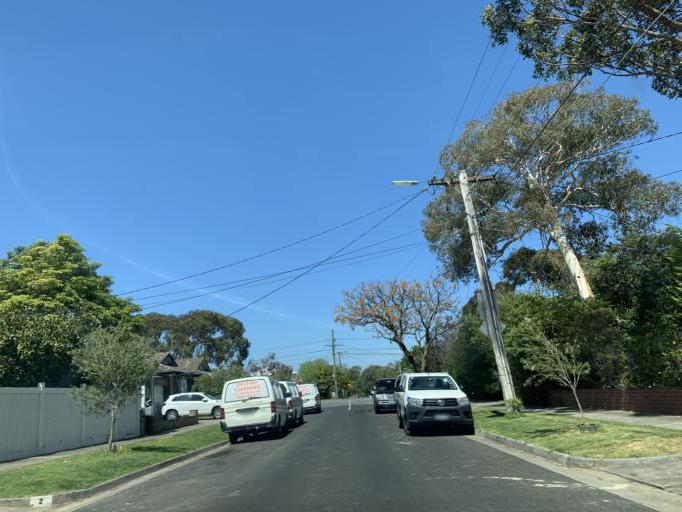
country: AU
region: Victoria
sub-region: Bayside
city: Hampton East
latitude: -37.9468
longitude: 145.0306
